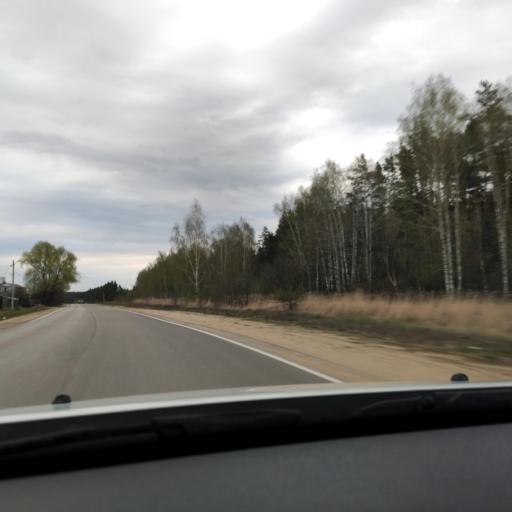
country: RU
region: Lipetsk
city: Zadonsk
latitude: 52.4189
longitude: 38.9378
